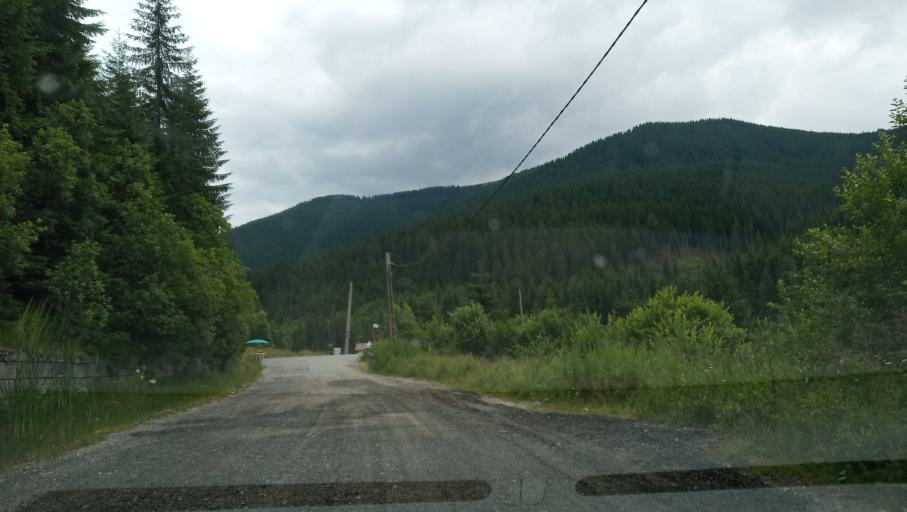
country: RO
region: Valcea
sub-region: Comuna Voineasa
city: Voineasa
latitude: 45.4249
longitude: 23.7645
